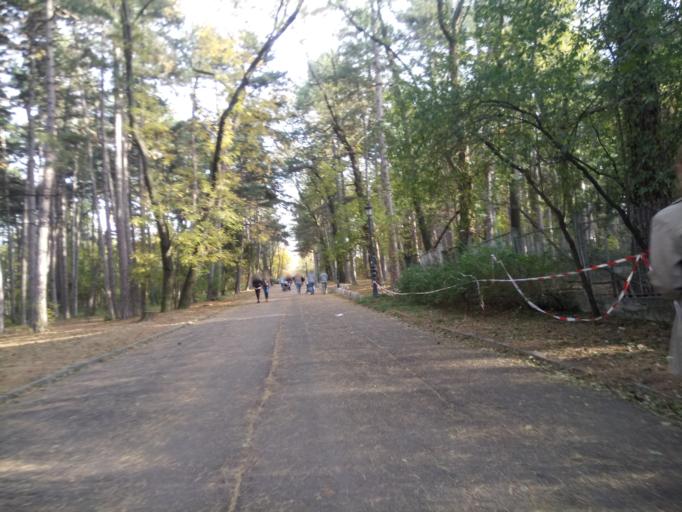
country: BG
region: Sofia-Capital
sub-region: Stolichna Obshtina
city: Sofia
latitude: 42.6835
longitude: 23.3429
